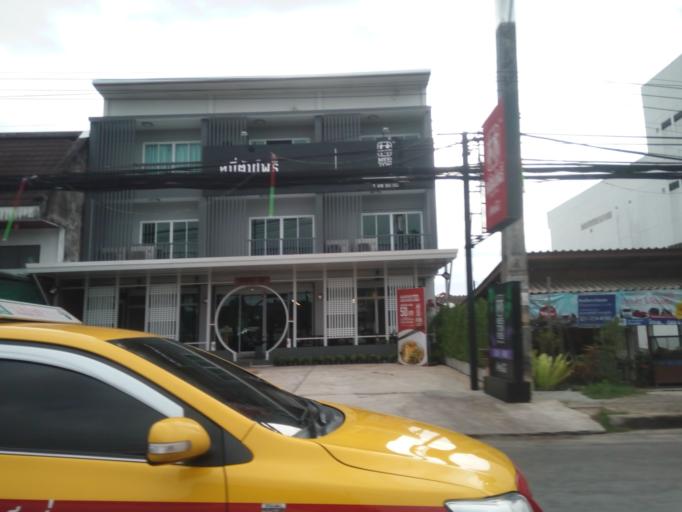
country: TH
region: Phuket
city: Thalang
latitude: 8.0231
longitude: 98.3345
